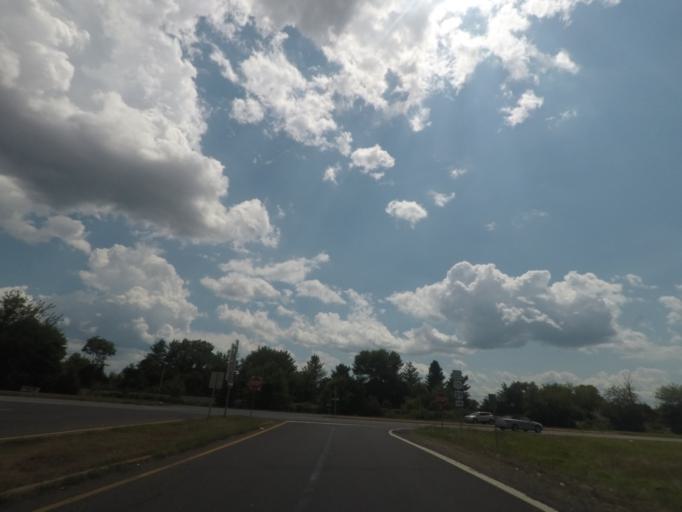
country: US
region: Virginia
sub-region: Culpeper County
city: Culpeper
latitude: 38.4890
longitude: -77.9392
